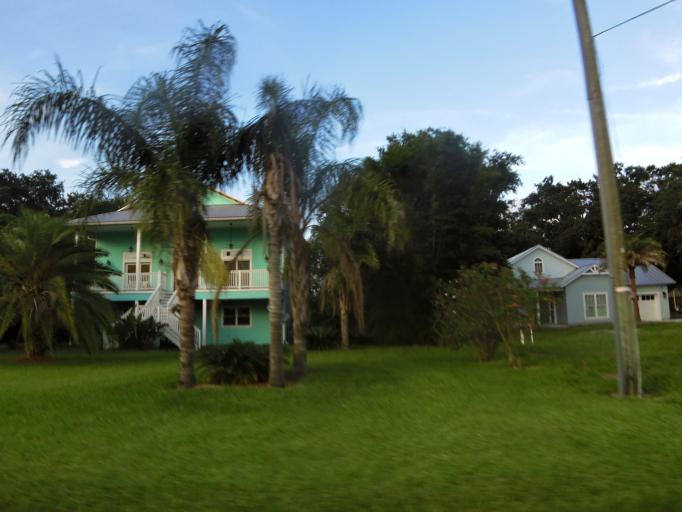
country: US
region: Florida
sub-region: Duval County
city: Atlantic Beach
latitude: 30.3965
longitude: -81.5038
